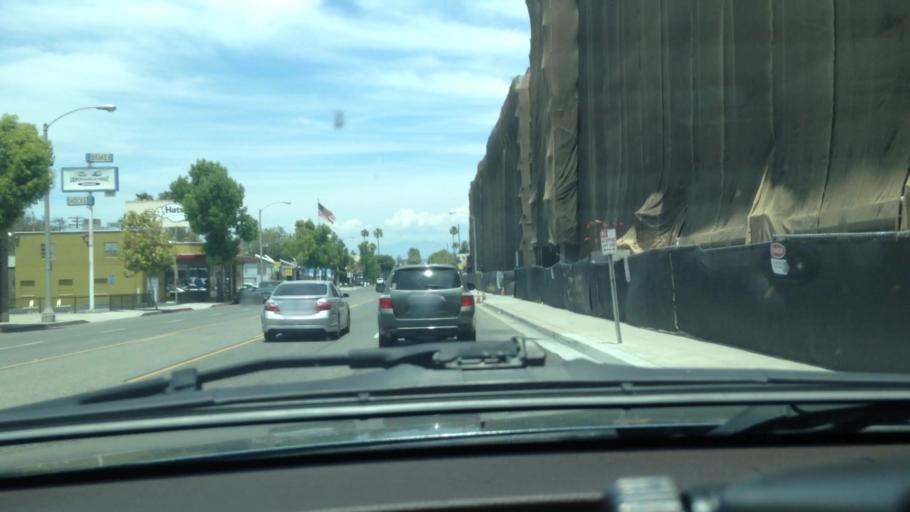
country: US
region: California
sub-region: Orange County
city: Fullerton
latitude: 33.8635
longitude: -117.9242
